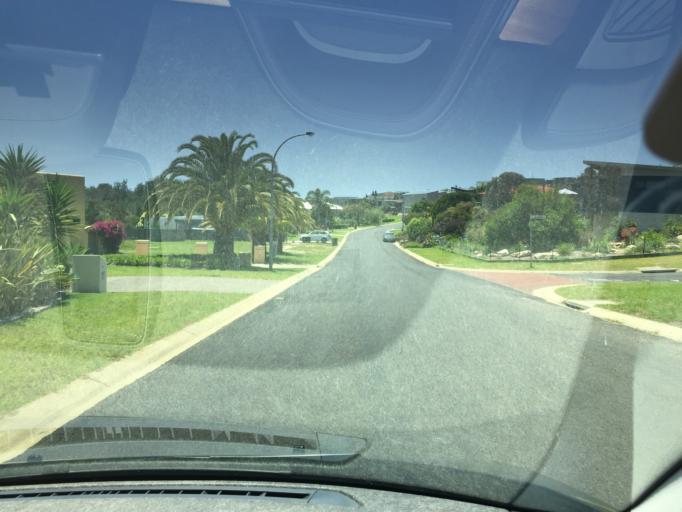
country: AU
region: New South Wales
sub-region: Bega Valley
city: Merimbula
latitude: -36.8492
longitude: 149.9317
